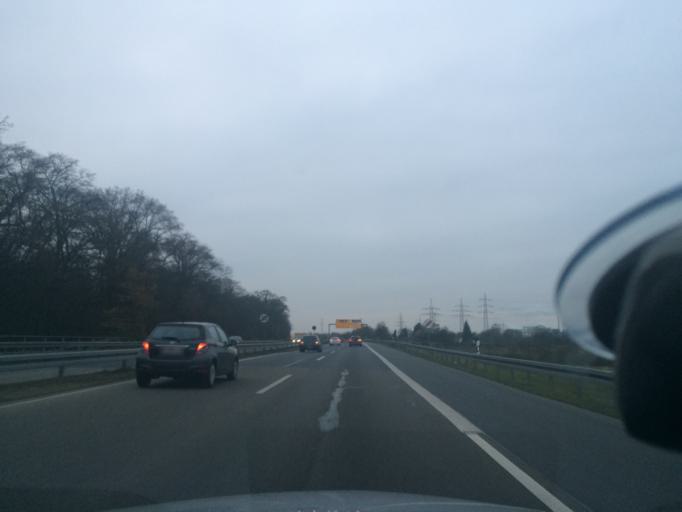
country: DE
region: Hesse
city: Kelsterbach
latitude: 50.0807
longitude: 8.5577
